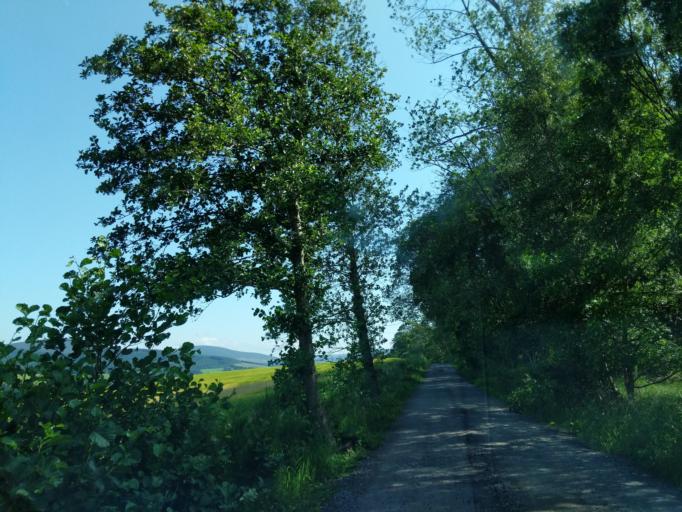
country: GB
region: Scotland
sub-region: Moray
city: Rothes
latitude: 57.4757
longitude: -3.2376
